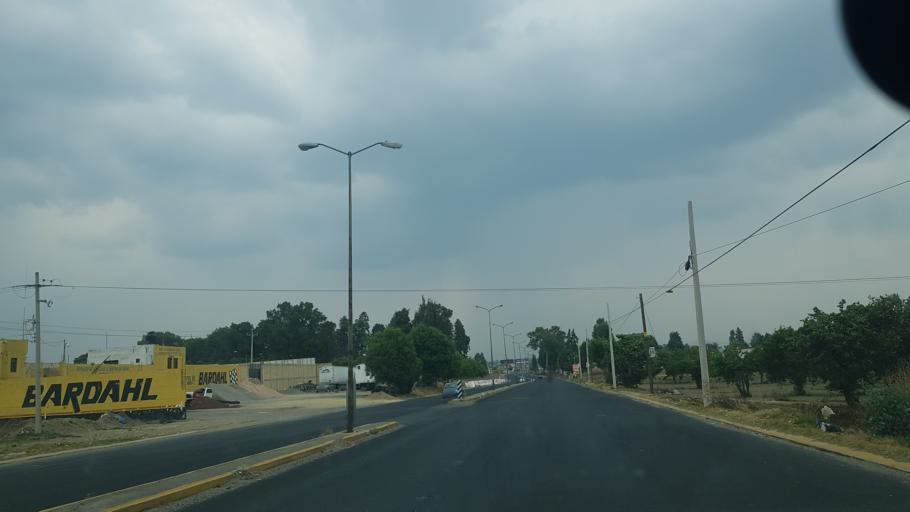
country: MX
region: Puebla
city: Huejotzingo
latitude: 19.1734
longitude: -98.4135
